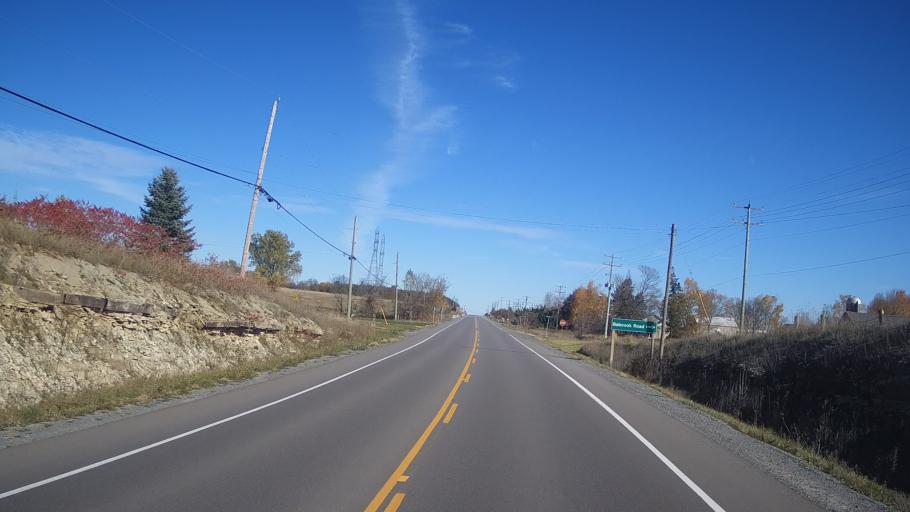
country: CA
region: Ontario
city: Kingston
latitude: 44.4050
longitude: -76.6489
